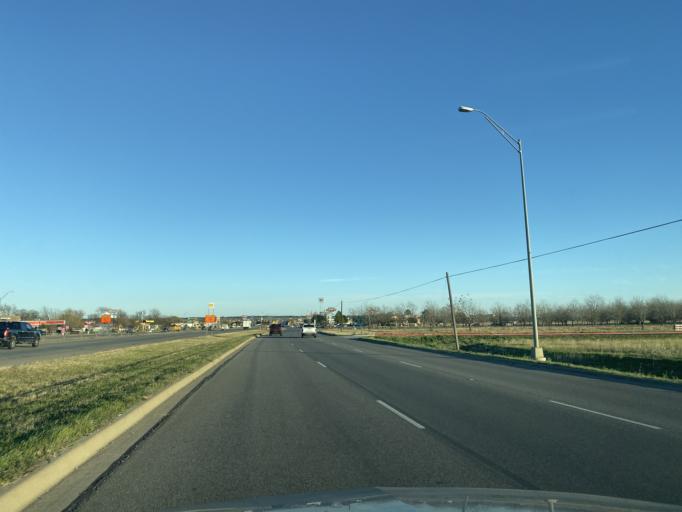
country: US
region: Texas
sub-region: Bastrop County
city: Bastrop
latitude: 30.1103
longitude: -97.3444
